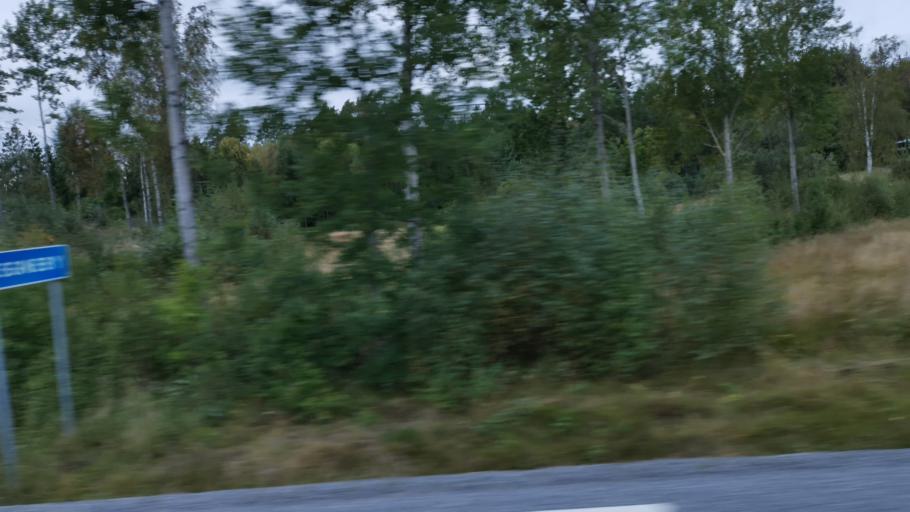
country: SE
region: Vaestra Goetaland
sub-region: Tanums Kommun
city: Tanumshede
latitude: 58.6934
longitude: 11.3367
